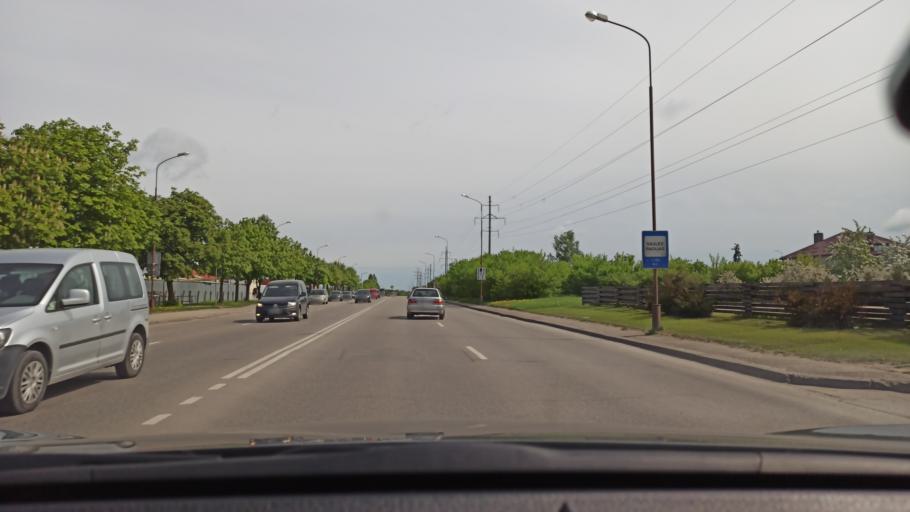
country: LT
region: Siauliu apskritis
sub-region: Siauliai
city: Siauliai
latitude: 55.9076
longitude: 23.3301
